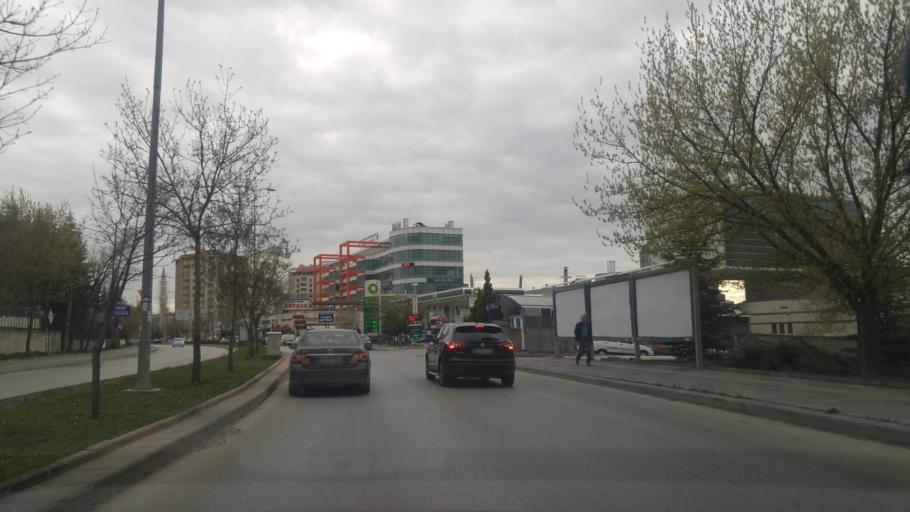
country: TR
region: Ankara
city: Etimesgut
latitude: 39.8770
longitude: 32.6874
